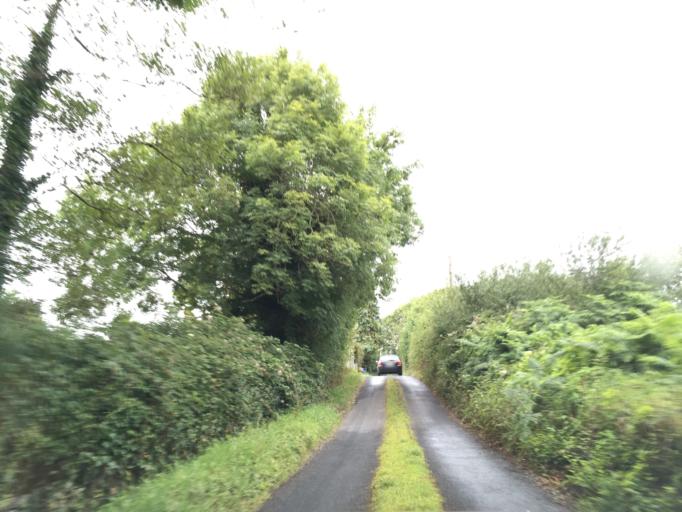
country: IE
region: Munster
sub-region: An Clar
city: Ennis
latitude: 52.7290
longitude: -9.0855
